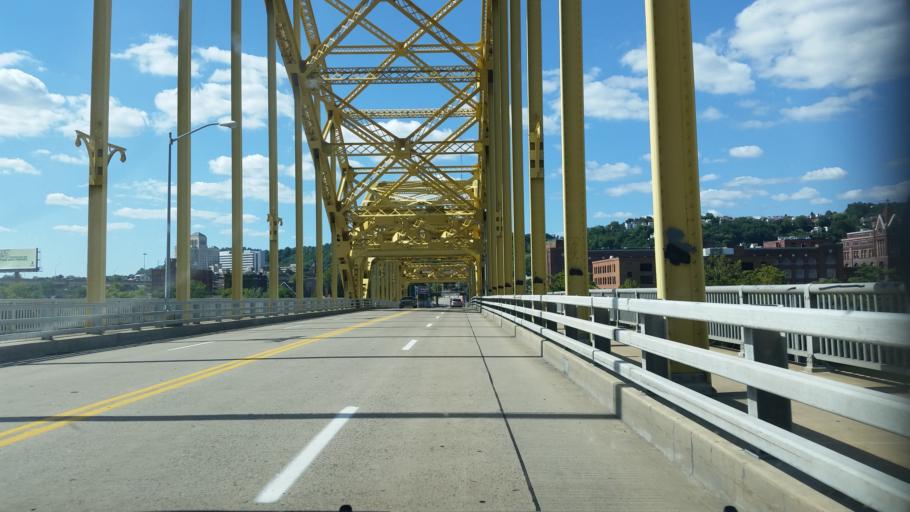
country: US
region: Pennsylvania
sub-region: Allegheny County
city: Pittsburgh
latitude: 40.4513
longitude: -79.9904
